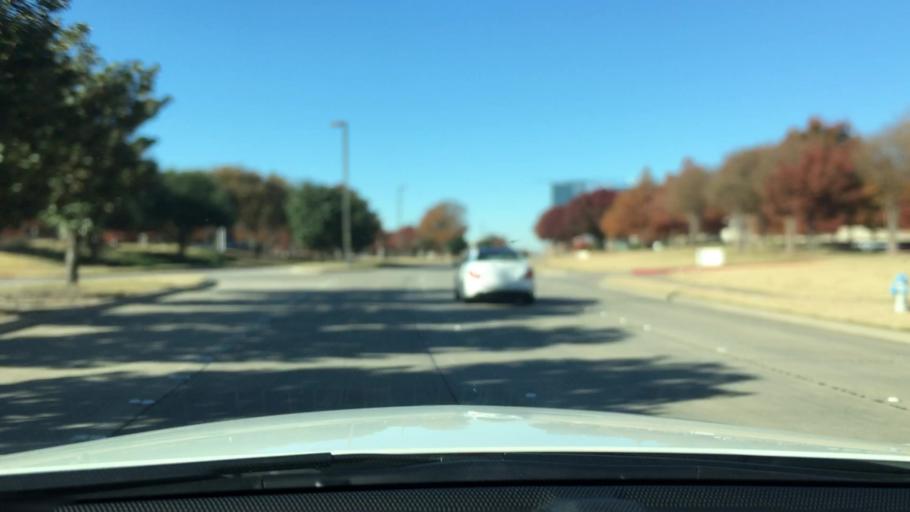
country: US
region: Texas
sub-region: Collin County
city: Frisco
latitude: 33.0842
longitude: -96.8139
